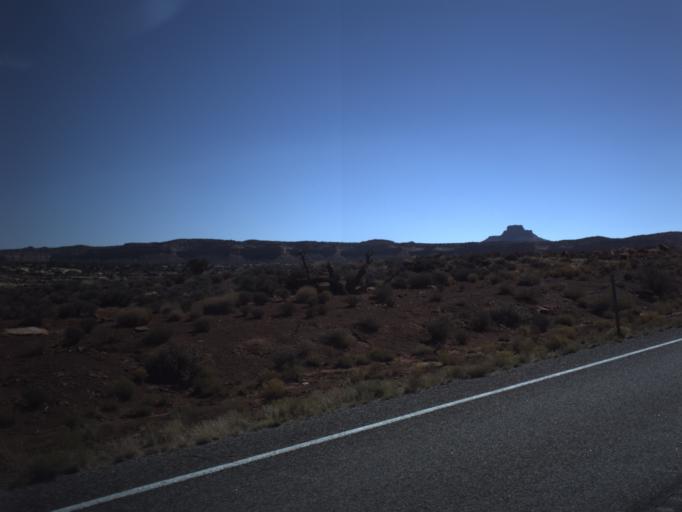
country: US
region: Utah
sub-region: San Juan County
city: Blanding
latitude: 37.7845
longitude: -110.2943
